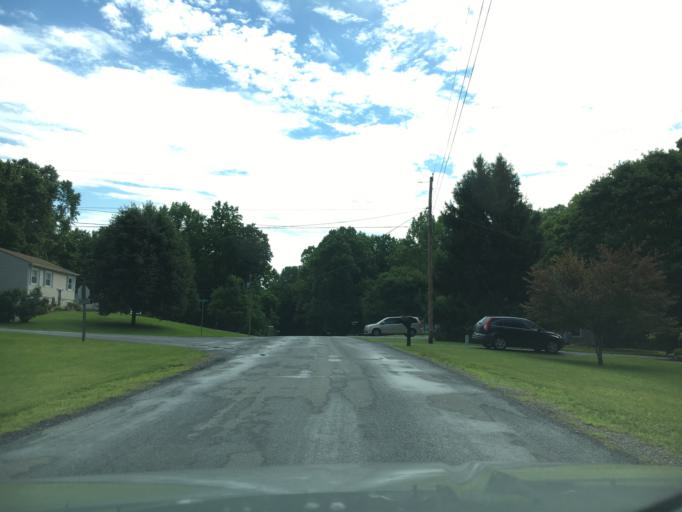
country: US
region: Virginia
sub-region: Bedford County
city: Forest
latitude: 37.3596
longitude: -79.2608
